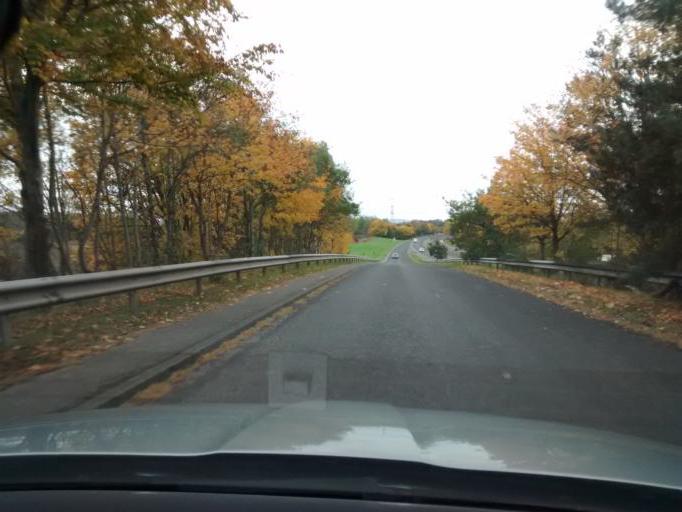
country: GB
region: Scotland
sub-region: Perth and Kinross
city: Luncarty
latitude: 56.4474
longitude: -3.4718
